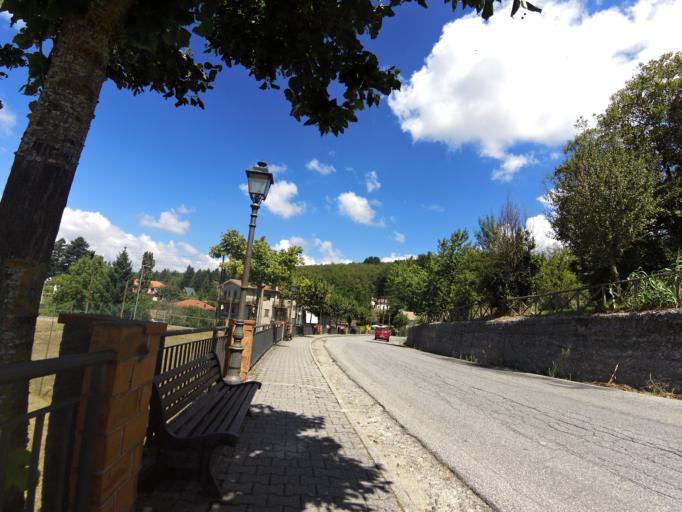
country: IT
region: Calabria
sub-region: Provincia di Vibo-Valentia
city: Mongiana
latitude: 38.5144
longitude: 16.3182
